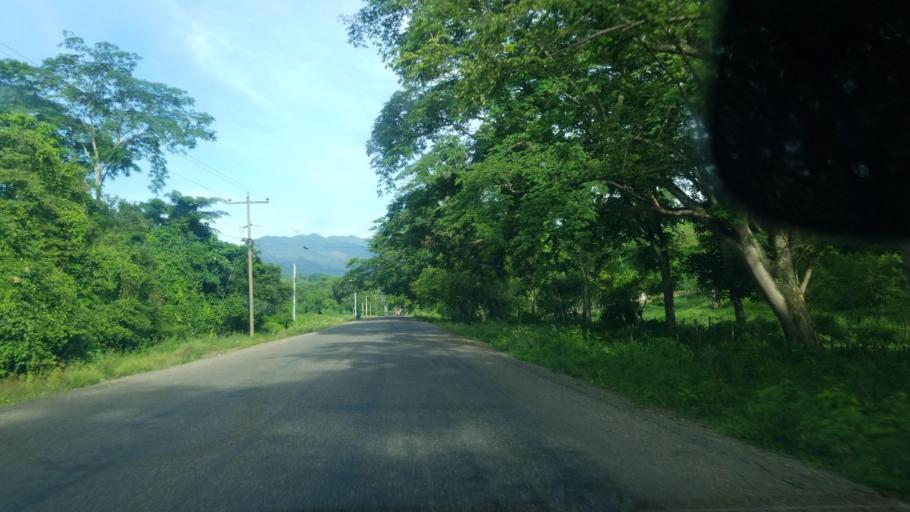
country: HN
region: Santa Barbara
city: Trinidad
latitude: 15.1330
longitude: -88.2154
